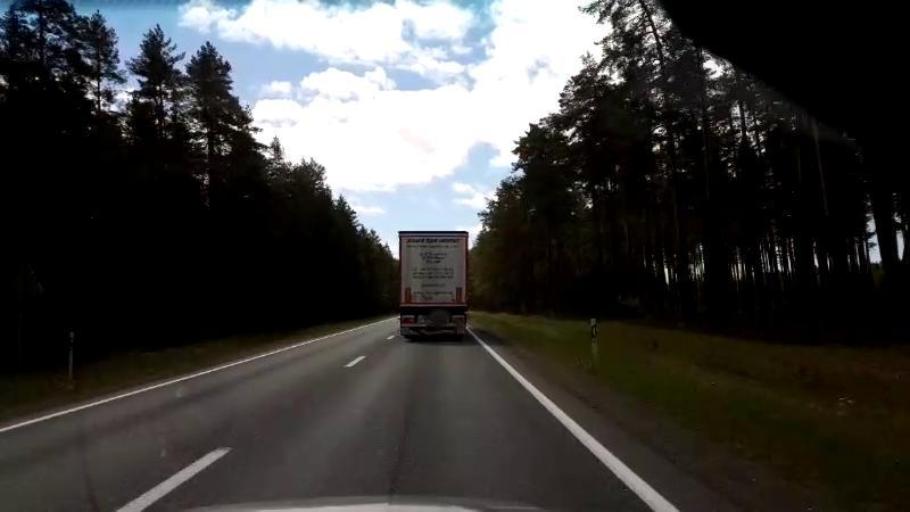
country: LV
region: Salacgrivas
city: Salacgriva
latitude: 57.5614
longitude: 24.4339
